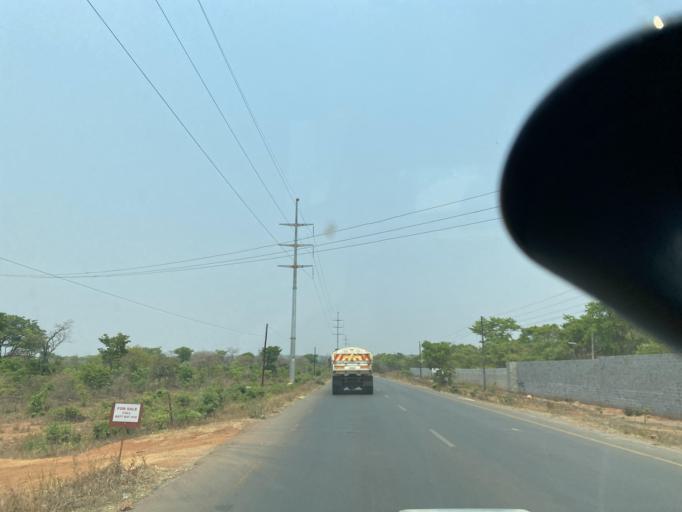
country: ZM
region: Lusaka
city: Lusaka
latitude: -15.5192
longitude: 28.4567
